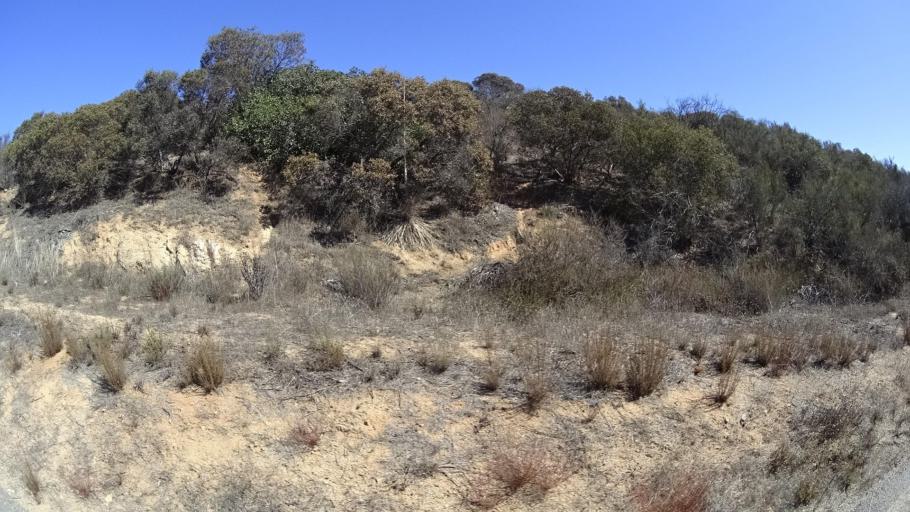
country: US
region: California
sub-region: San Diego County
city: Alpine
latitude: 32.8005
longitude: -116.7712
